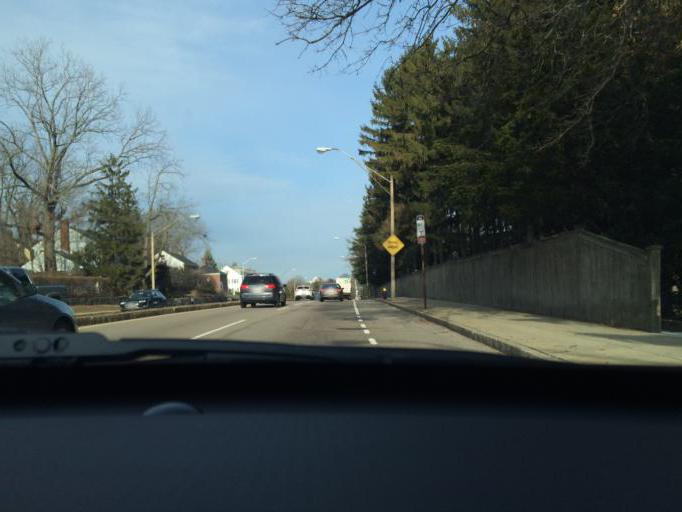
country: US
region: Massachusetts
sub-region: Suffolk County
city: Jamaica Plain
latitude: 42.3064
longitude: -71.1240
